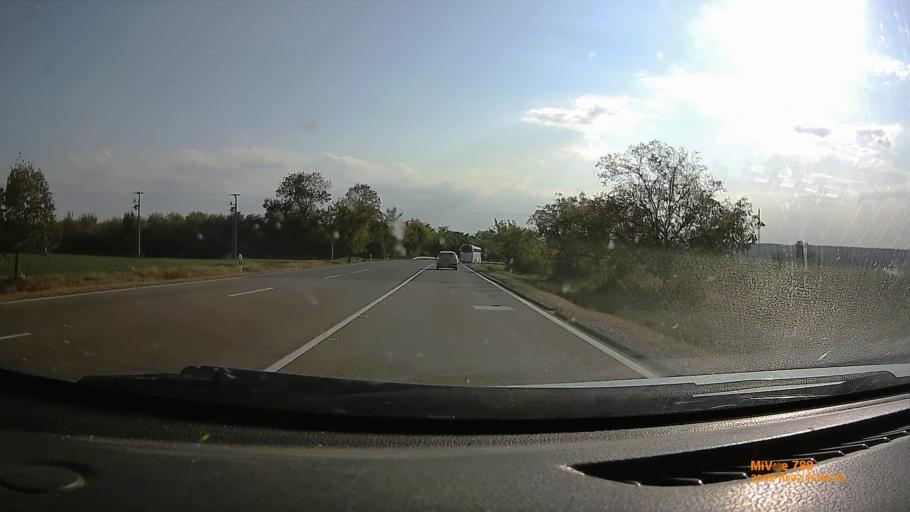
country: HU
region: Heves
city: Kerecsend
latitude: 47.8011
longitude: 20.3554
